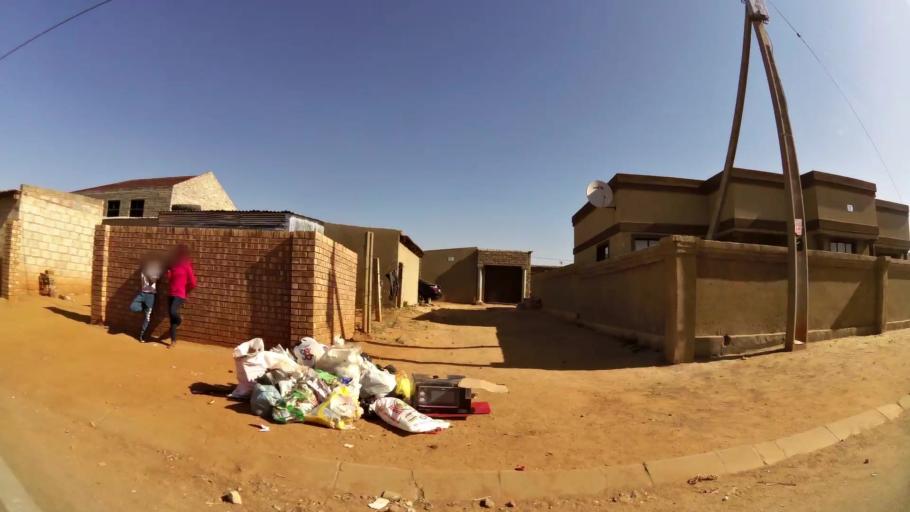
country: ZA
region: Gauteng
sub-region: Ekurhuleni Metropolitan Municipality
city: Tembisa
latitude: -26.0254
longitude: 28.2380
